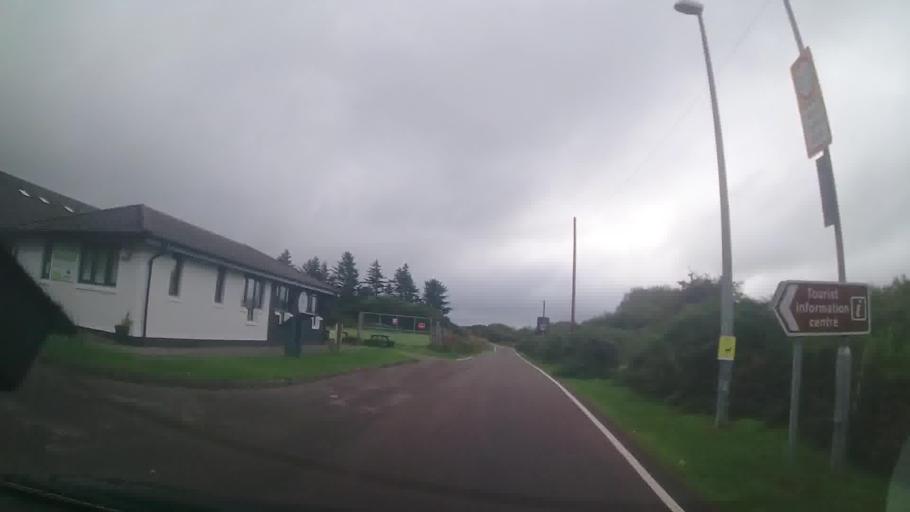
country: GB
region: Scotland
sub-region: Argyll and Bute
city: Isle Of Mull
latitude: 56.6965
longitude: -6.1004
